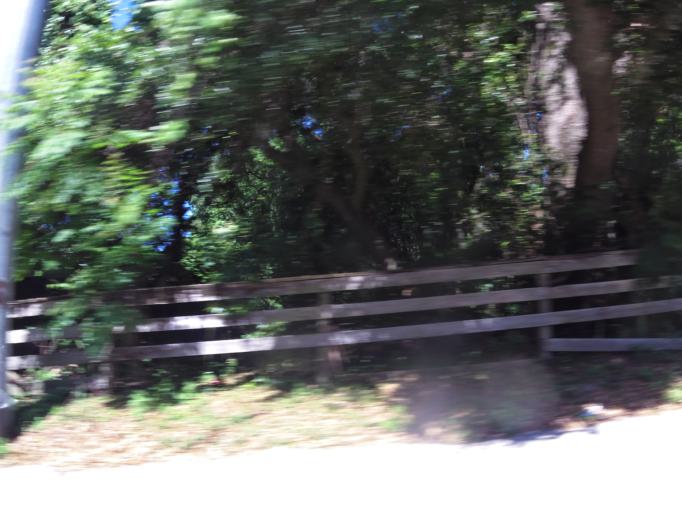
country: US
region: Florida
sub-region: Duval County
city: Jacksonville
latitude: 30.3260
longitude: -81.5851
